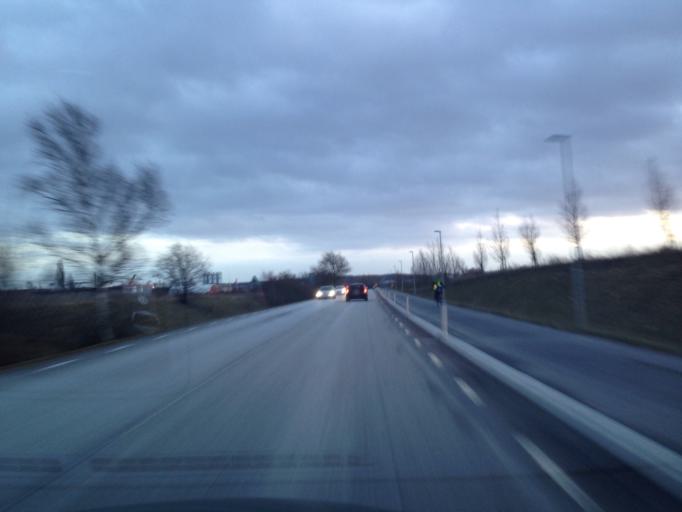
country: SE
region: Skane
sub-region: Burlovs Kommun
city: Arloev
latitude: 55.6194
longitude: 13.0806
